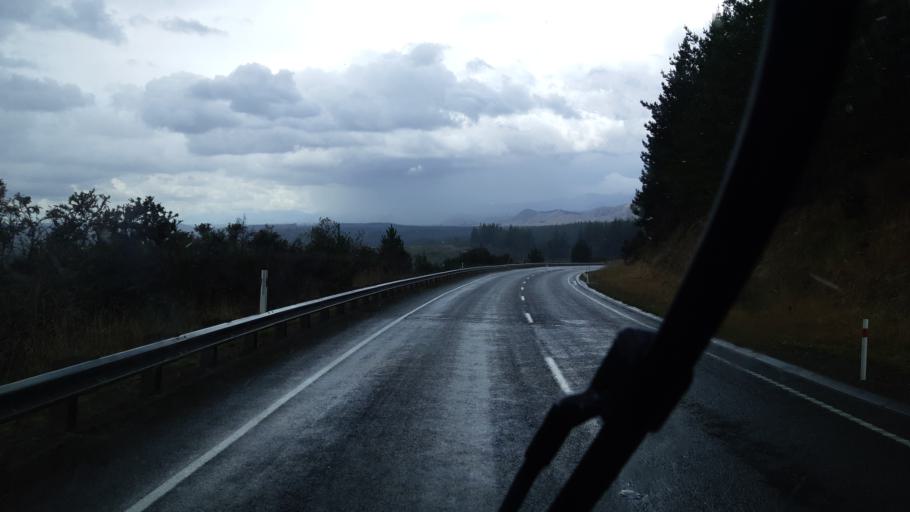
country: NZ
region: Tasman
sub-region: Tasman District
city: Wakefield
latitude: -41.4791
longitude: 172.9194
